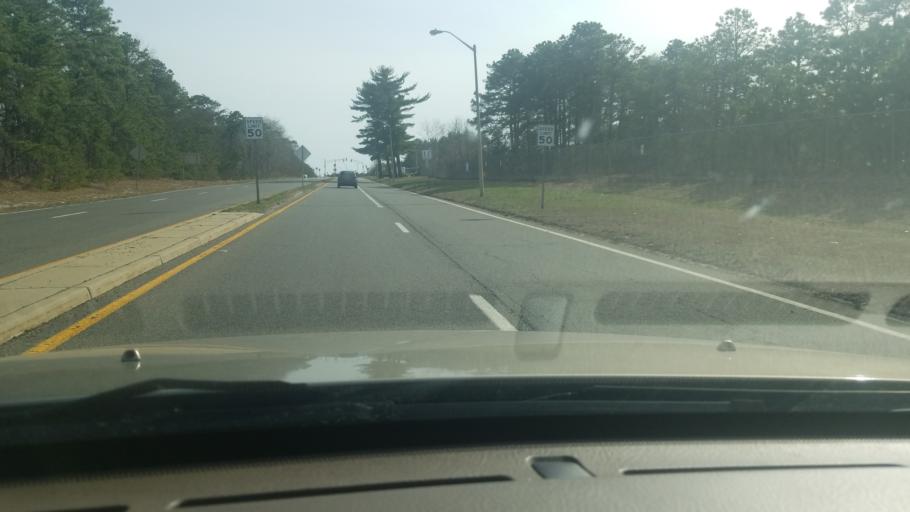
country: US
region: New Jersey
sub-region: Ocean County
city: Lakehurst
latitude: 40.0284
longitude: -74.3075
